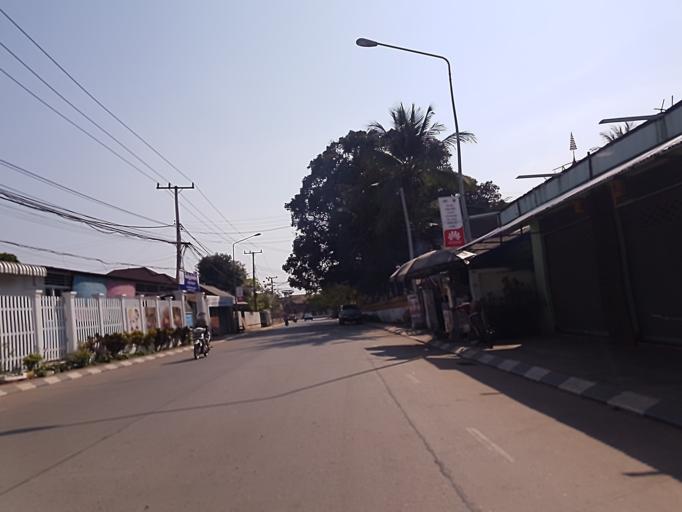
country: LA
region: Vientiane
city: Vientiane
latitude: 17.9462
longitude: 102.6388
